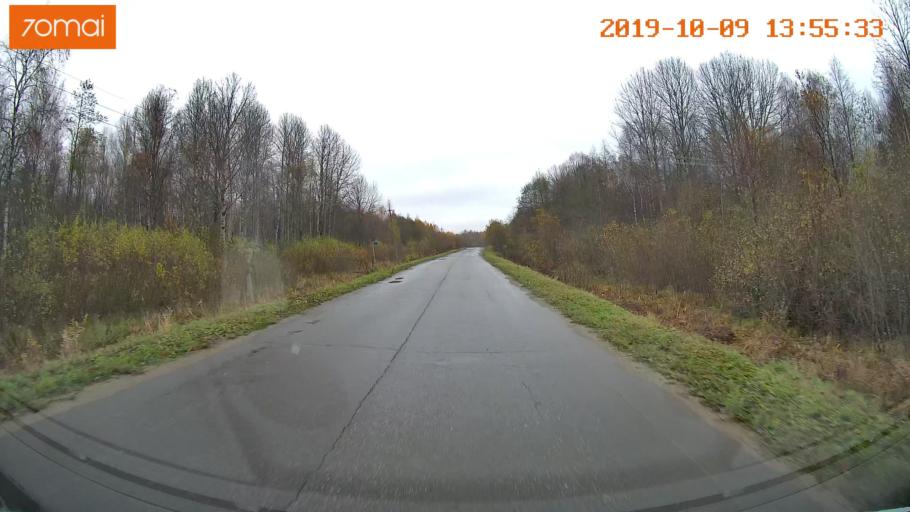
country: RU
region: Kostroma
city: Buy
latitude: 58.4252
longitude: 41.2752
